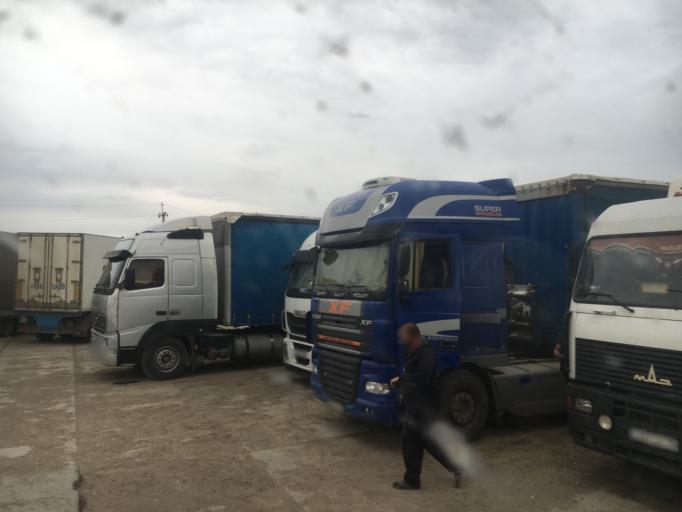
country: KZ
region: Batys Qazaqstan
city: Oral
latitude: 51.2667
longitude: 51.4081
